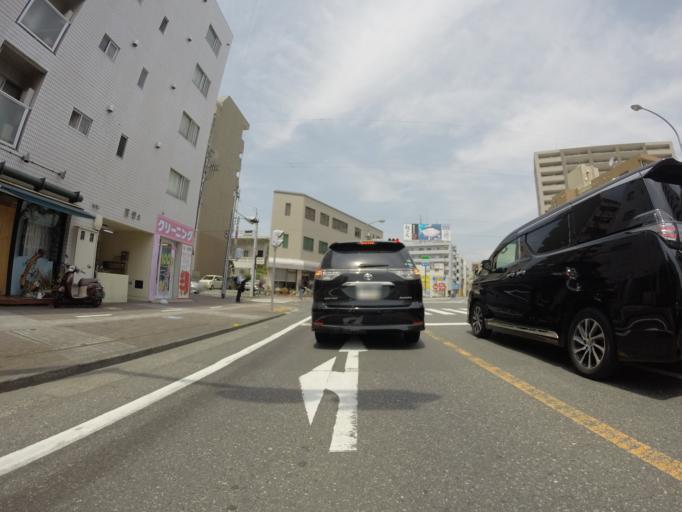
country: JP
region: Shizuoka
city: Shizuoka-shi
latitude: 34.9779
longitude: 138.3778
